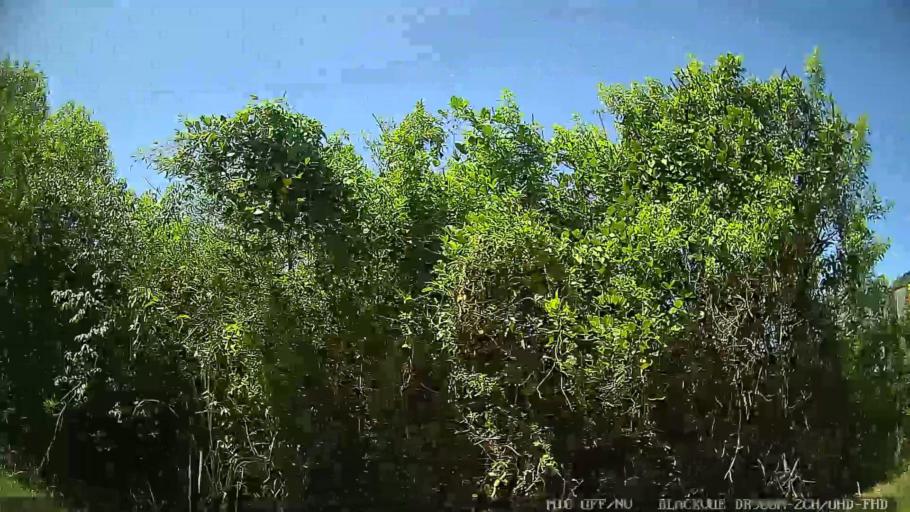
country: BR
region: Sao Paulo
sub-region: Peruibe
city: Peruibe
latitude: -24.3302
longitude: -47.0047
